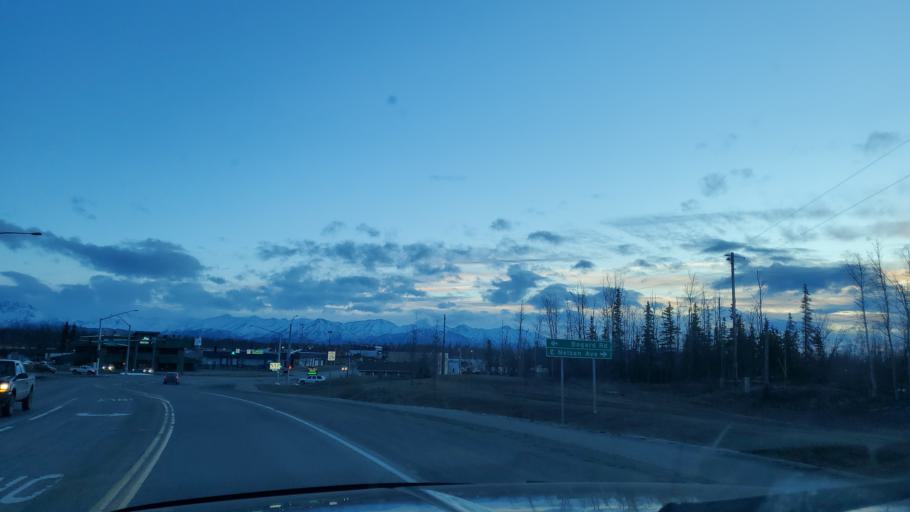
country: US
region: Alaska
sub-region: Matanuska-Susitna Borough
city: Wasilla
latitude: 61.5862
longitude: -149.4430
